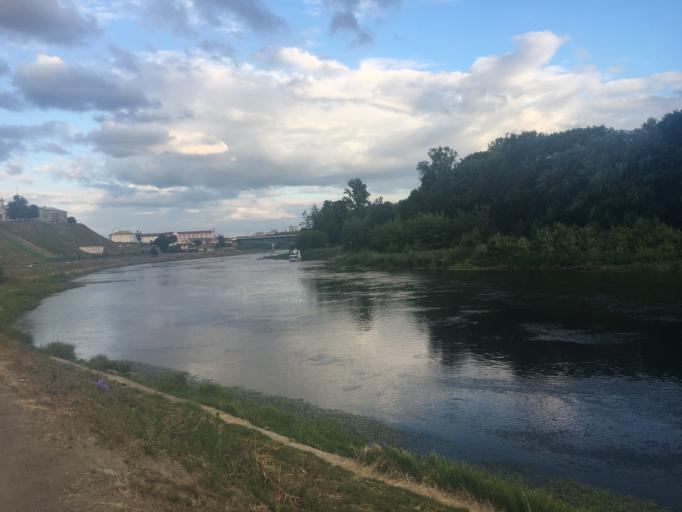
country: BY
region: Grodnenskaya
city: Hrodna
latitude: 53.6781
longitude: 23.8180
